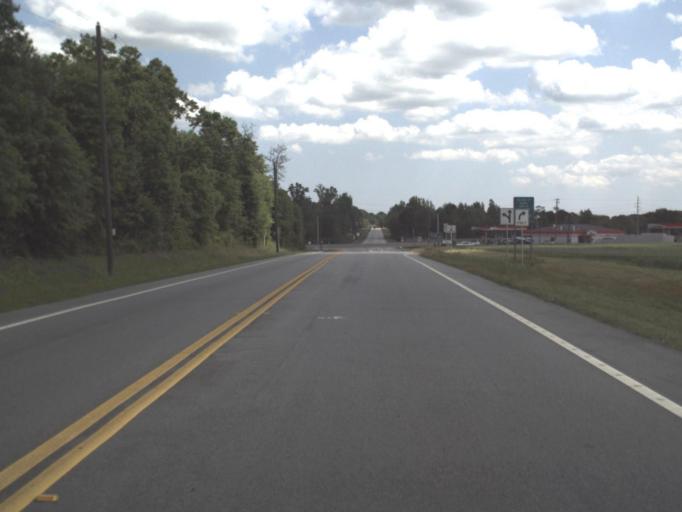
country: US
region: Florida
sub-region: Escambia County
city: Molino
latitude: 30.7335
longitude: -87.3516
